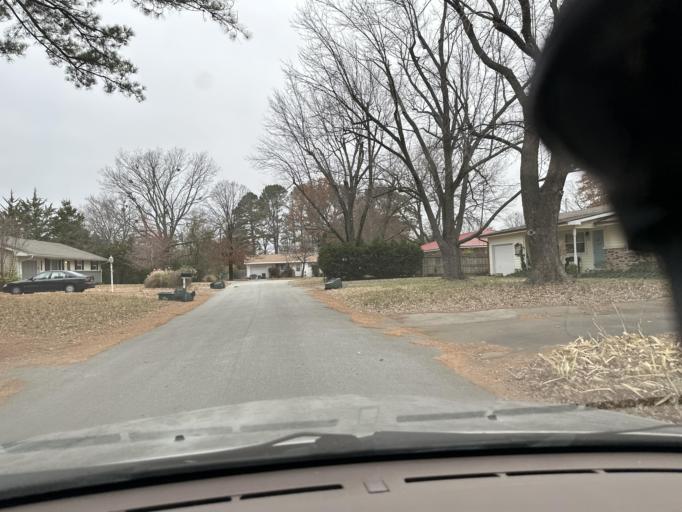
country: US
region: Arkansas
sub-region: Washington County
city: Johnson
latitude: 36.1120
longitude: -94.1423
